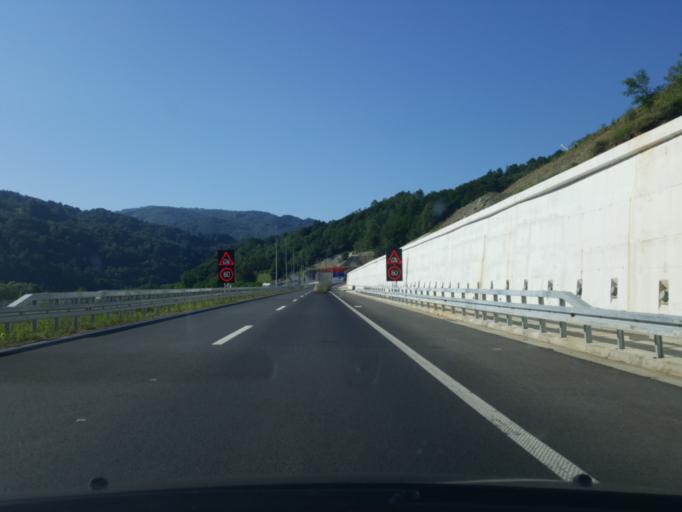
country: RS
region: Central Serbia
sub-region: Jablanicki Okrug
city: Vlasotince
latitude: 42.8482
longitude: 22.1295
